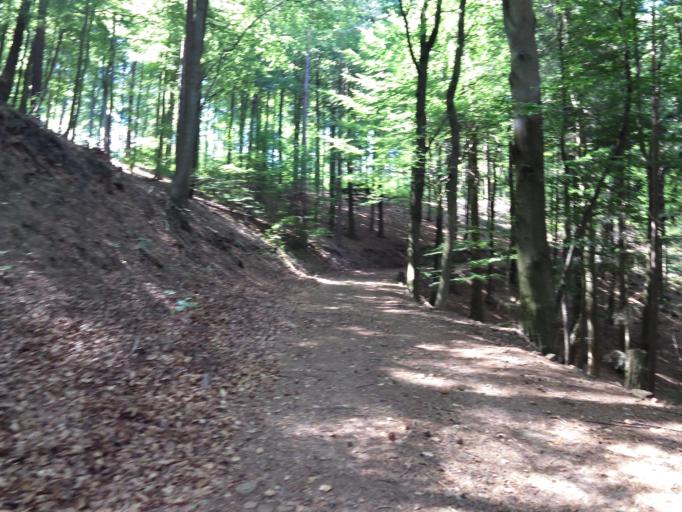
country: DE
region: Rheinland-Pfalz
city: Waldleiningen
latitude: 49.3750
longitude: 7.8589
